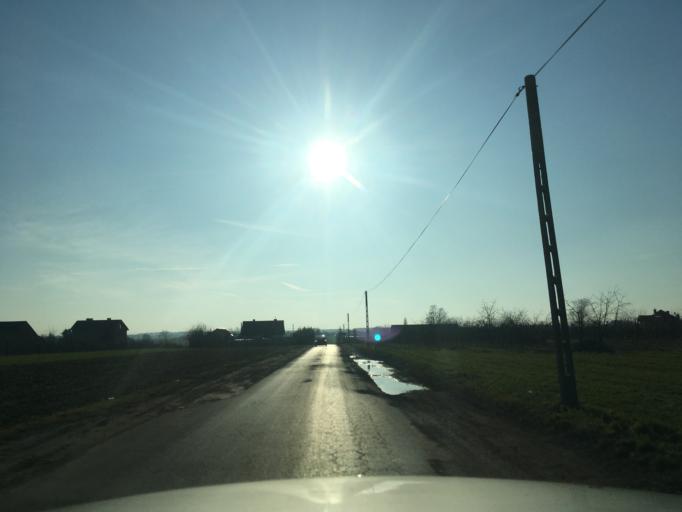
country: PL
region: Masovian Voivodeship
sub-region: Powiat piaseczynski
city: Tarczyn
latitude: 52.0384
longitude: 20.8233
